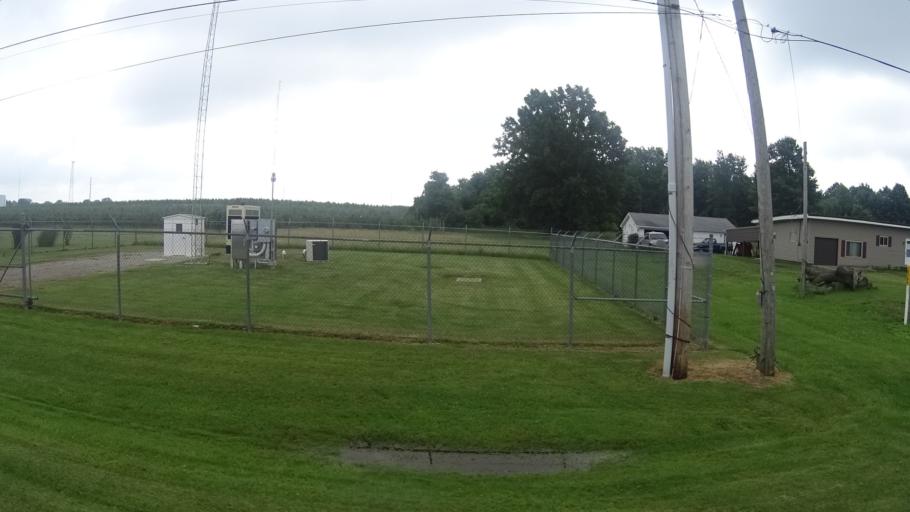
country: US
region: Ohio
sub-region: Huron County
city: Wakeman
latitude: 41.3002
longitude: -82.4927
